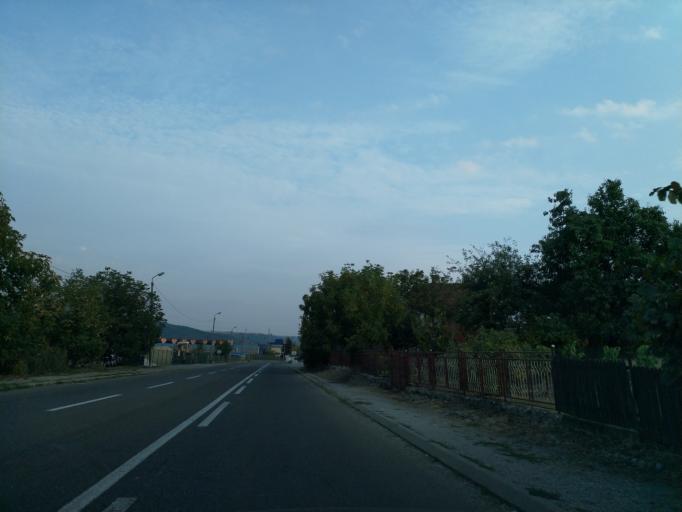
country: RS
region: Central Serbia
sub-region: Sumadijski Okrug
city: Topola
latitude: 44.2476
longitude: 20.6905
